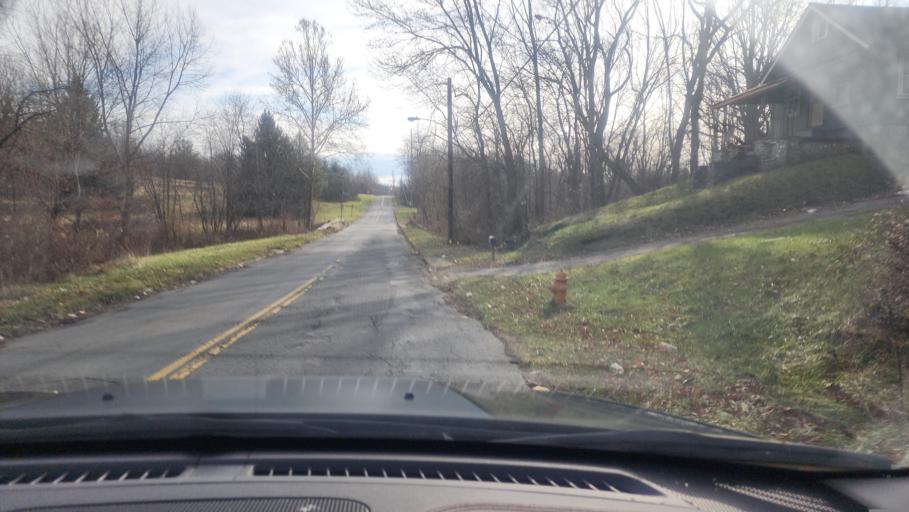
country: US
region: Ohio
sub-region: Mahoning County
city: Campbell
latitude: 41.1036
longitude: -80.6162
